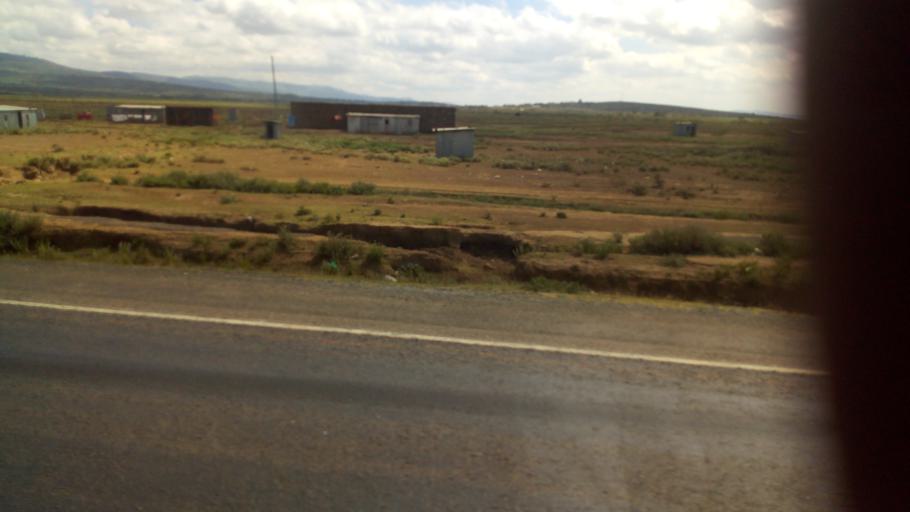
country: KE
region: Narok
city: Narok
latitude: -1.1071
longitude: 36.2351
